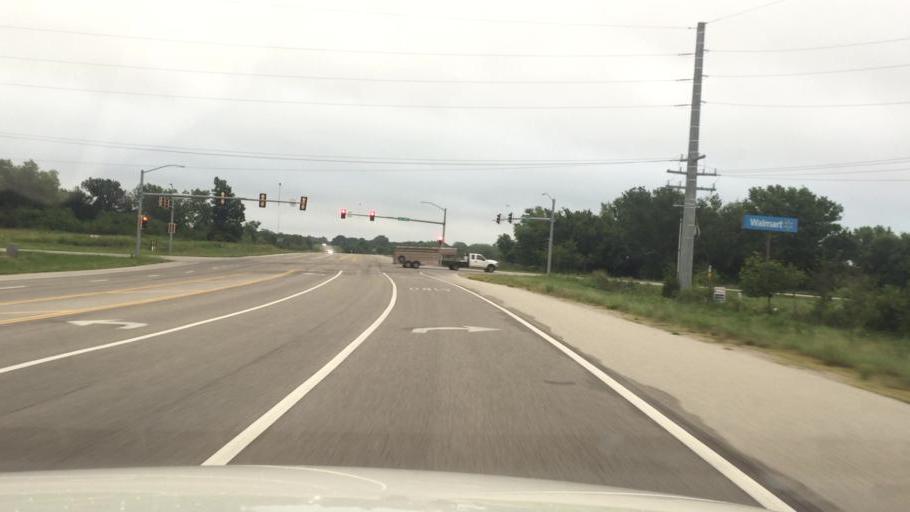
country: US
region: Kansas
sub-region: Montgomery County
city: Coffeyville
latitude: 37.0449
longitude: -95.5788
